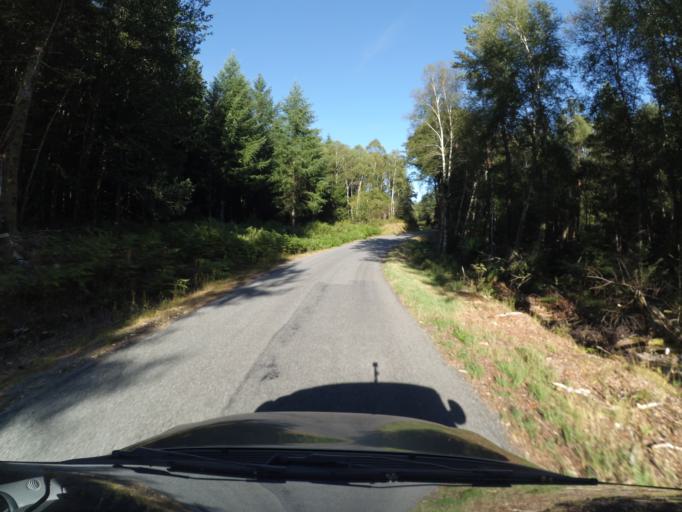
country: FR
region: Limousin
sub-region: Departement de la Creuse
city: Banize
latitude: 45.7892
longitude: 1.9583
